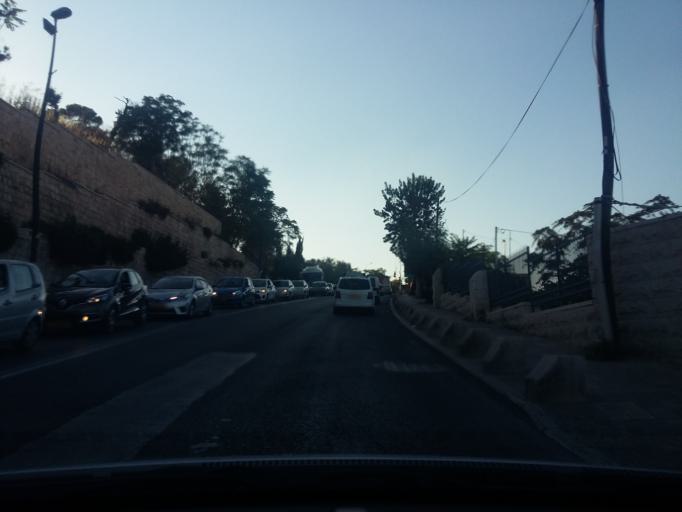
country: PS
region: West Bank
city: East Jerusalem
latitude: 31.7828
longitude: 35.2382
